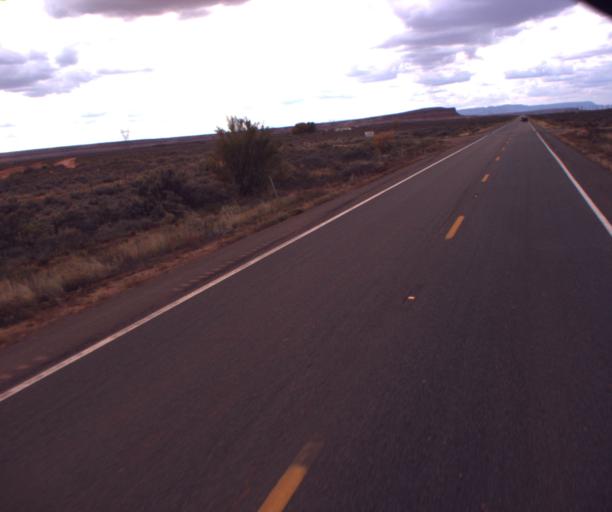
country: US
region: Arizona
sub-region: Navajo County
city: Kayenta
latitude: 36.8189
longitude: -109.8804
